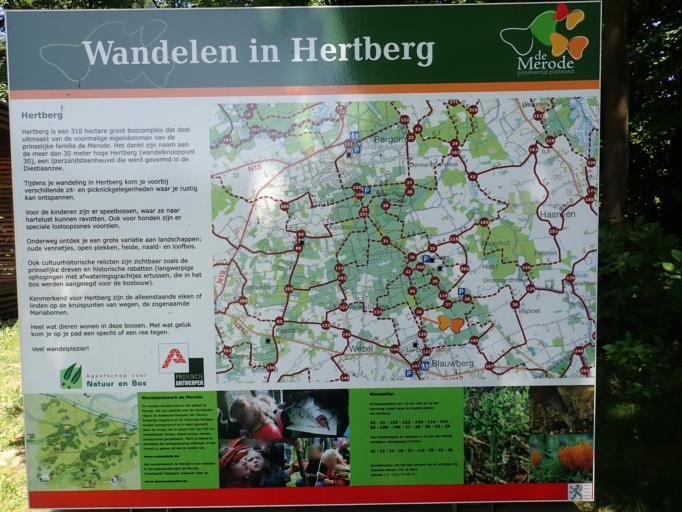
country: BE
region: Flanders
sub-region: Provincie Antwerpen
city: Westerlo
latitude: 51.0518
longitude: 4.9306
